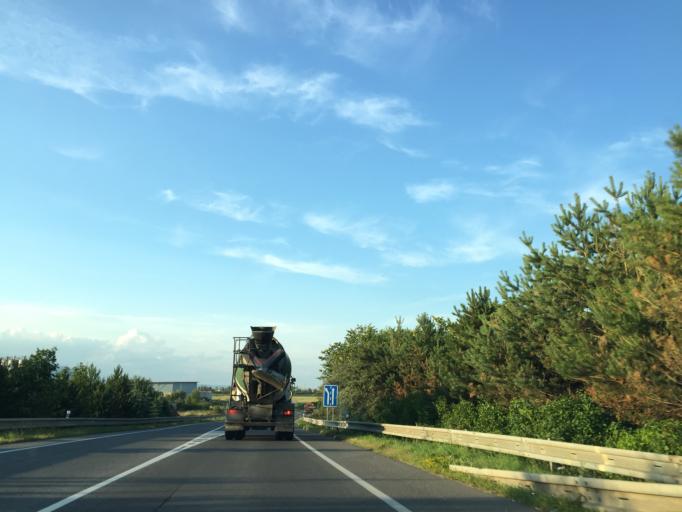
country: SK
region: Presovsky
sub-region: Okres Poprad
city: Poprad
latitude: 49.0662
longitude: 20.2696
